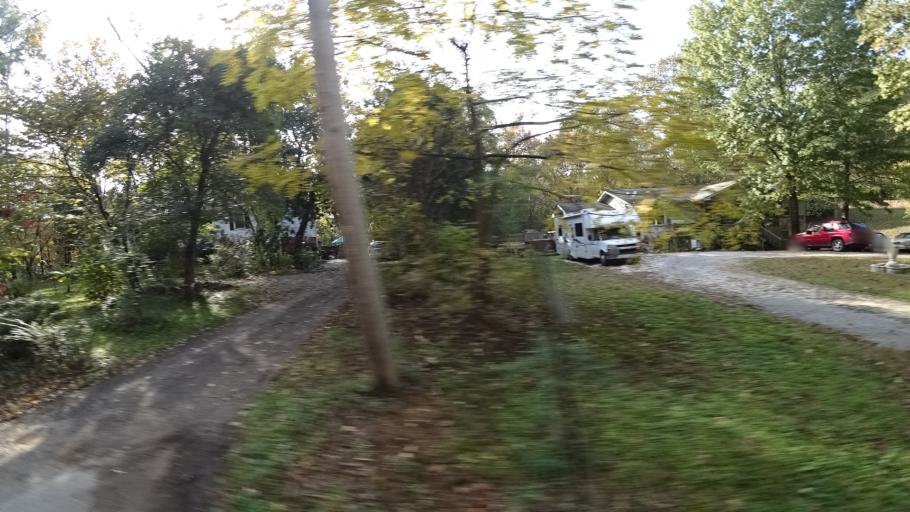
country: US
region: Tennessee
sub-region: Knox County
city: Farragut
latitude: 35.9136
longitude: -84.1868
